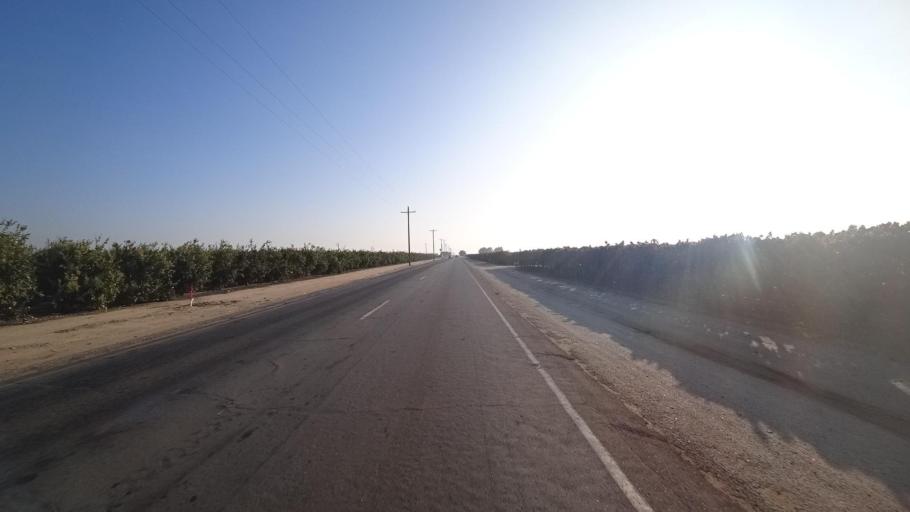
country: US
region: California
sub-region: Kern County
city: Delano
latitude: 35.7905
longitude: -119.1951
